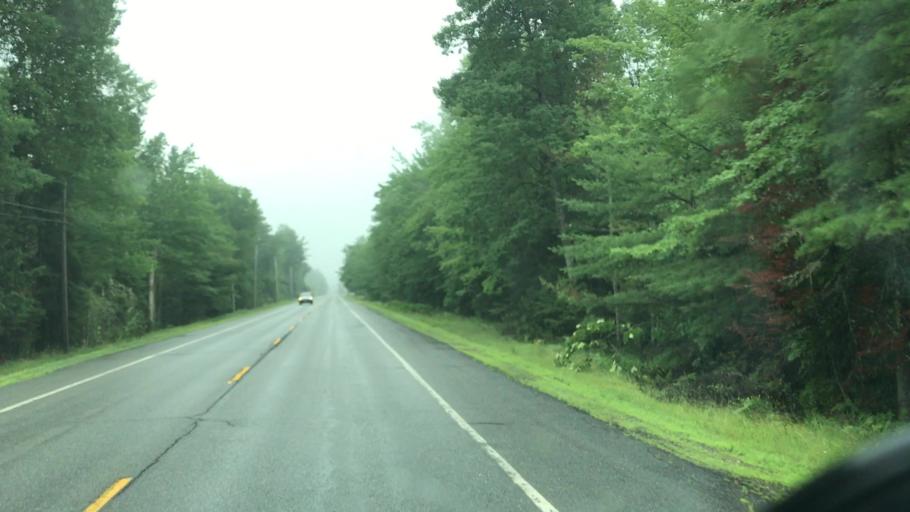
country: US
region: Maine
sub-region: Penobscot County
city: Howland
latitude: 45.2443
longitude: -68.6404
